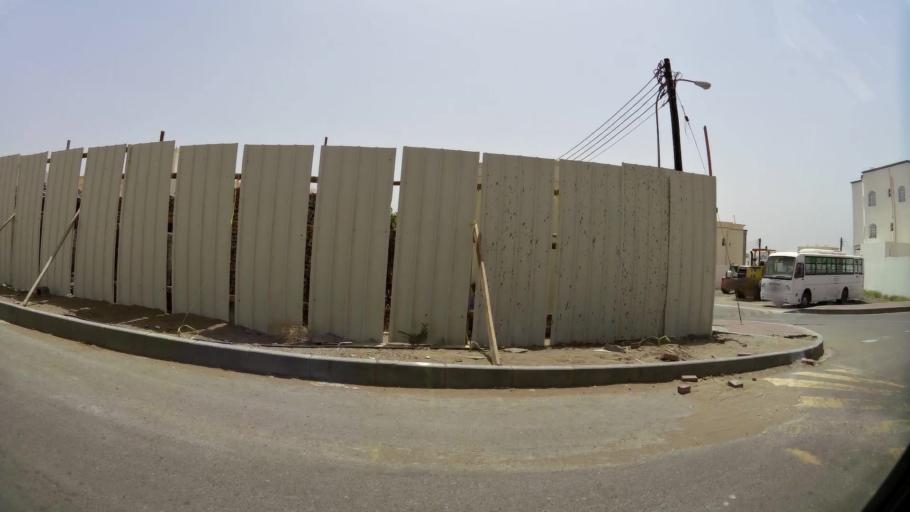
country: OM
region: Muhafazat Masqat
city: Bawshar
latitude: 23.5342
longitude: 58.3859
